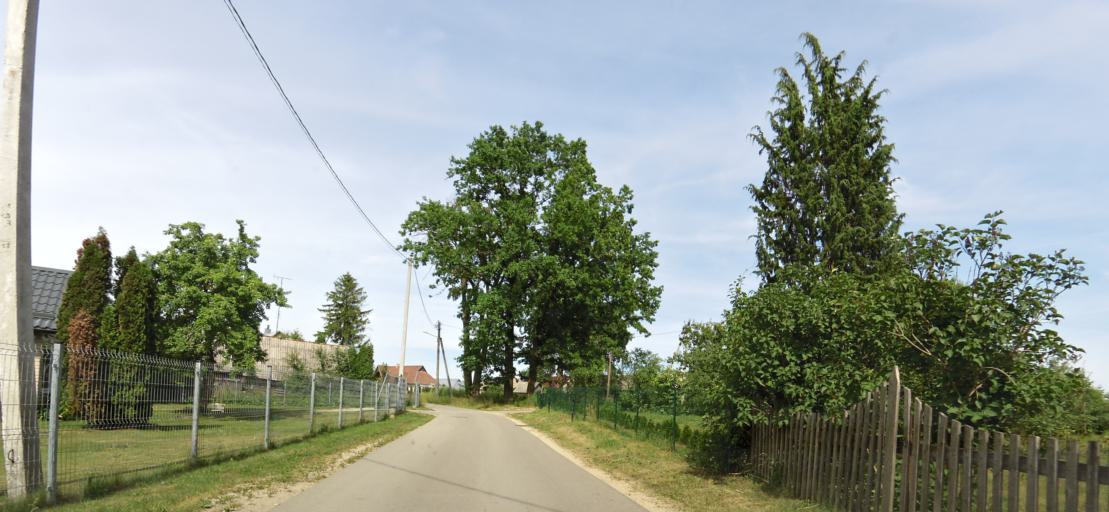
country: LT
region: Panevezys
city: Pasvalys
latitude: 55.9323
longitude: 24.3460
